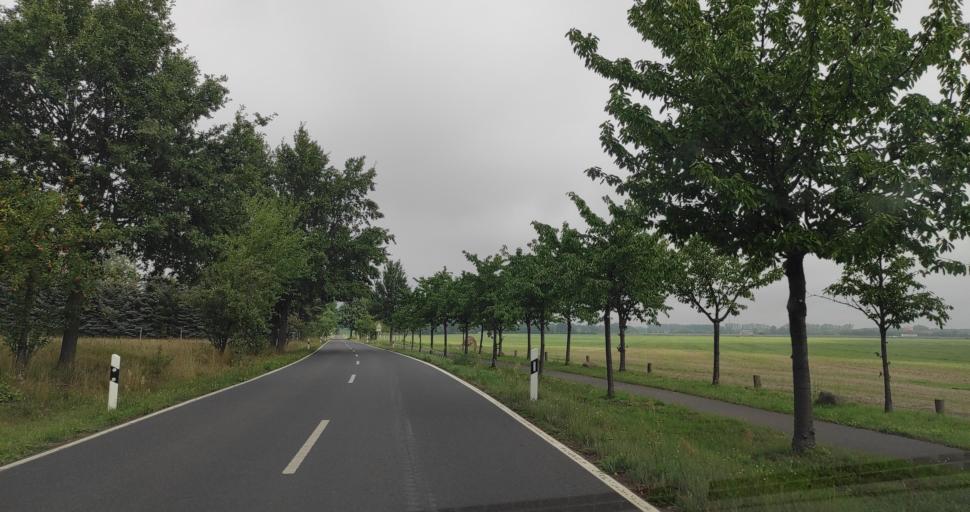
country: DE
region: Brandenburg
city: Forst
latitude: 51.6986
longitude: 14.6281
